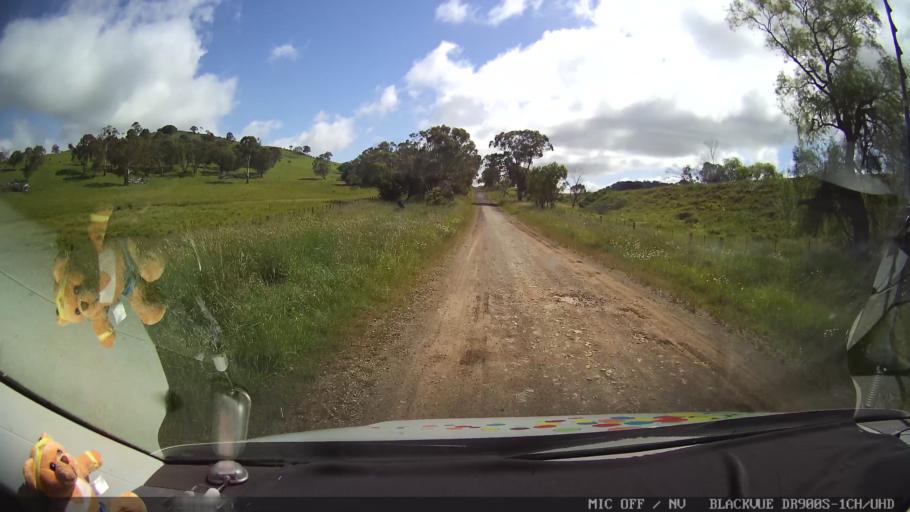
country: AU
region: New South Wales
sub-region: Guyra
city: Guyra
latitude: -30.0103
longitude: 151.6606
